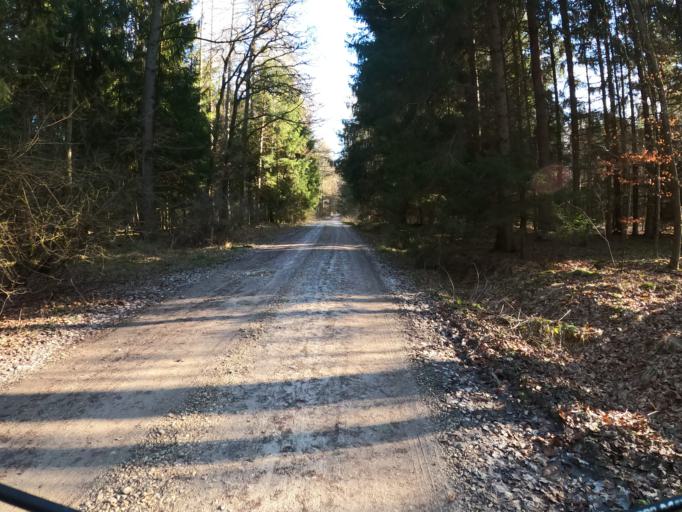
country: DE
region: Bavaria
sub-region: Swabia
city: Bubesheim
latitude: 48.4237
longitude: 10.2292
